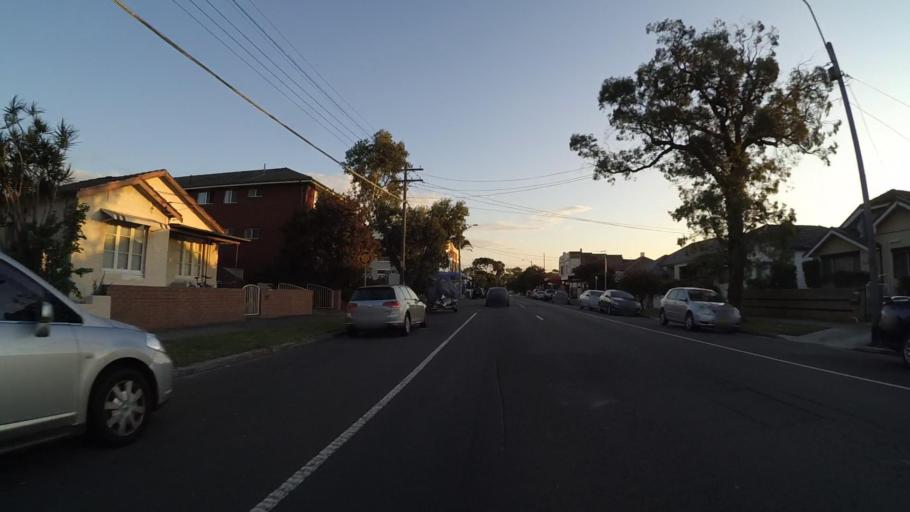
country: AU
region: New South Wales
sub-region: Botany Bay
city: Mascot
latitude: -33.9301
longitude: 151.2055
